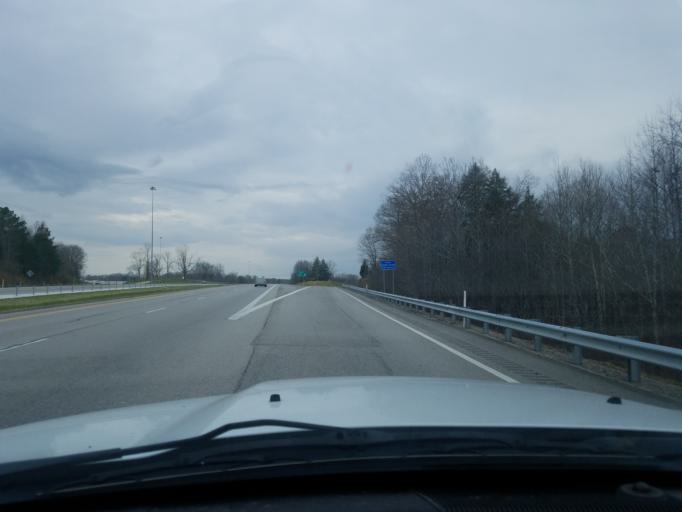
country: US
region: Kentucky
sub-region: Rowan County
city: Morehead
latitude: 38.1944
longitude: -83.4742
